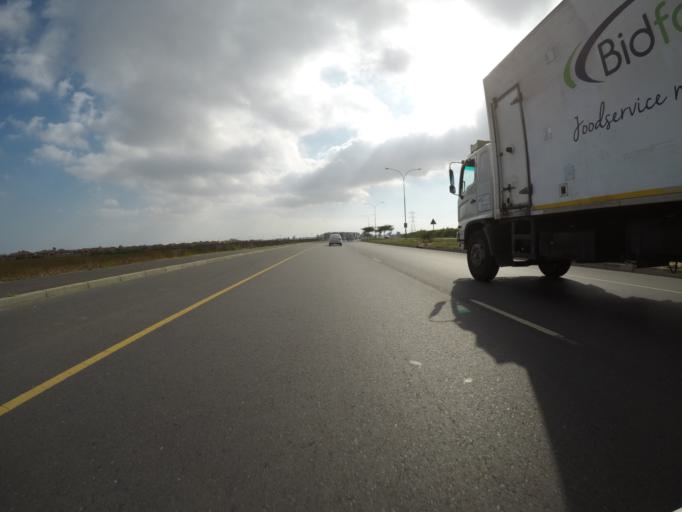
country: ZA
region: Western Cape
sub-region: City of Cape Town
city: Kraaifontein
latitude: -33.9565
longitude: 18.6850
